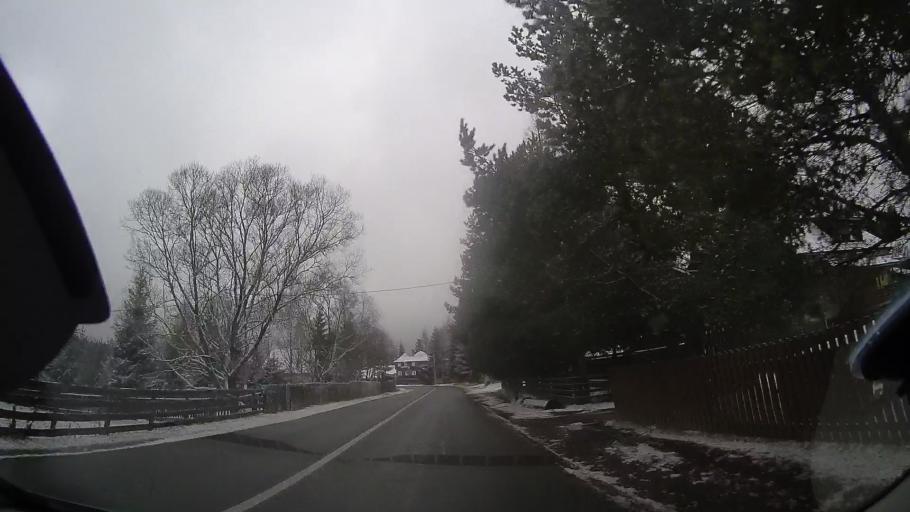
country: RO
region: Cluj
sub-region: Comuna Belis
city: Belis
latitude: 46.6810
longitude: 23.0367
